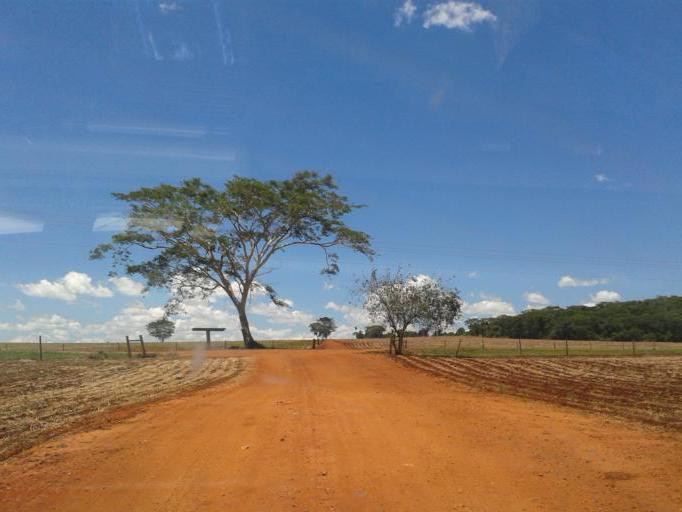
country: BR
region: Minas Gerais
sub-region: Capinopolis
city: Capinopolis
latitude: -18.6126
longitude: -49.5298
